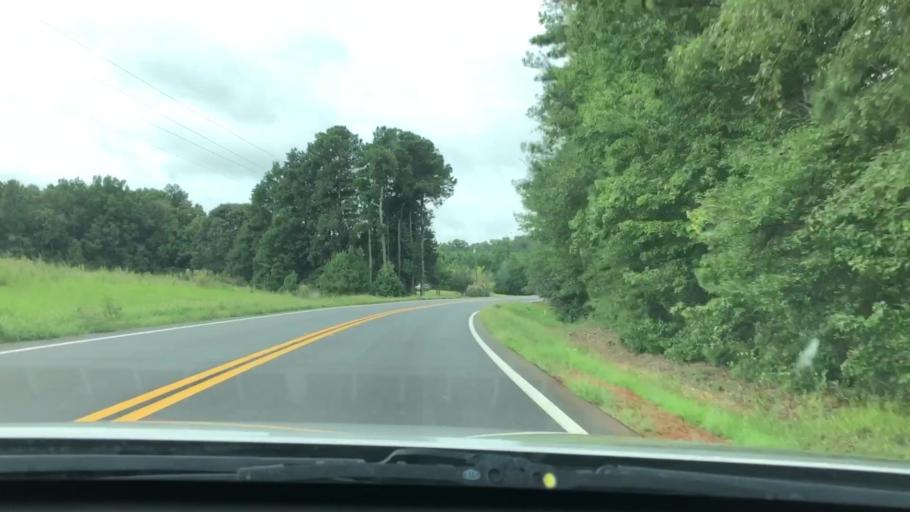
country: US
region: Georgia
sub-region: Pike County
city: Zebulon
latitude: 33.0254
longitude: -84.3901
